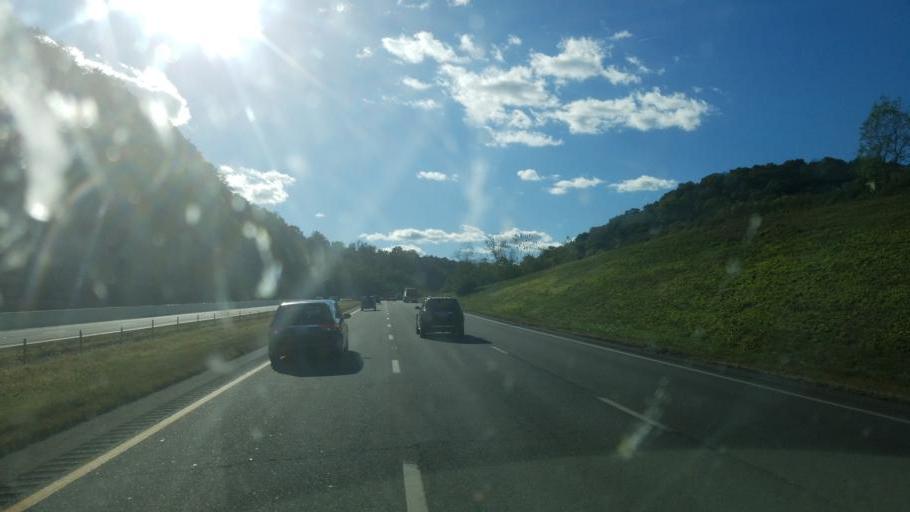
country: US
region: Ohio
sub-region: Belmont County
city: Bridgeport
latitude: 40.0466
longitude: -80.7494
